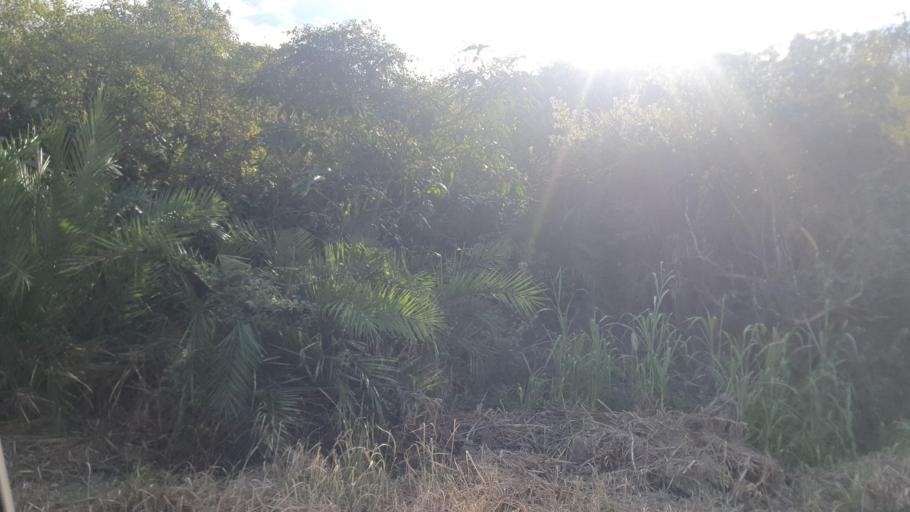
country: TW
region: Taiwan
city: Yujing
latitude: 23.0228
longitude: 120.3959
